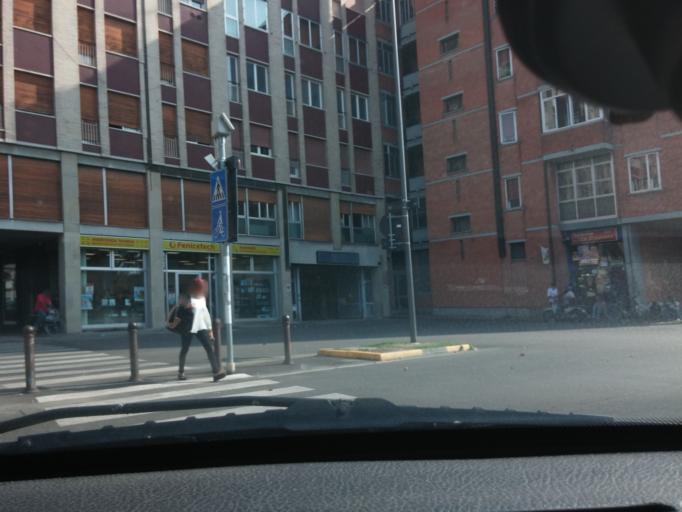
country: IT
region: Emilia-Romagna
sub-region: Provincia di Ferrara
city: Ferrara
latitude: 44.8425
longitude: 11.6043
